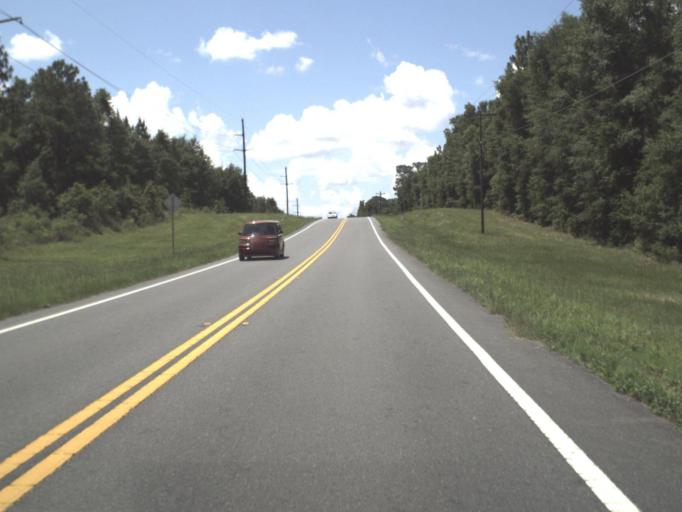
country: US
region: Florida
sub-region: Alachua County
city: Hawthorne
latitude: 29.6389
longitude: -82.0319
